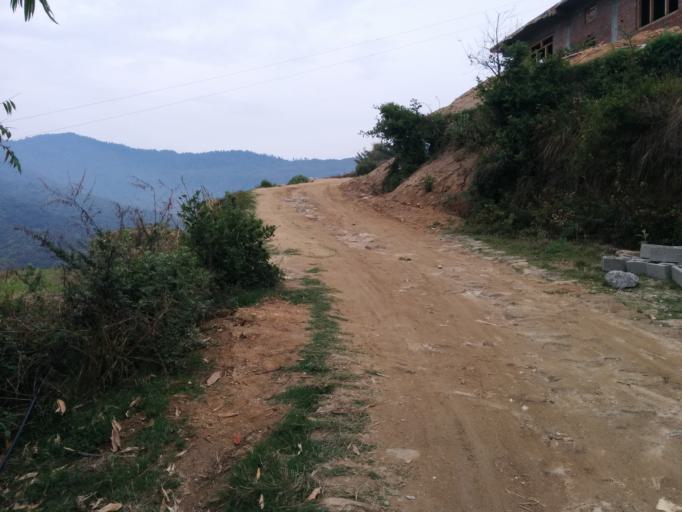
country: NP
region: Central Region
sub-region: Bagmati Zone
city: Bhaktapur
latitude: 27.7743
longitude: 85.4288
